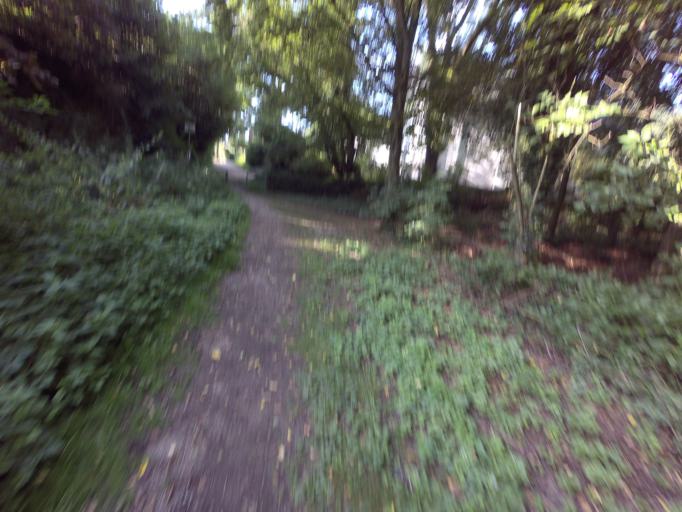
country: DE
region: North Rhine-Westphalia
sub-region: Regierungsbezirk Koln
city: Alsdorf
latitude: 50.8599
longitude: 6.1588
